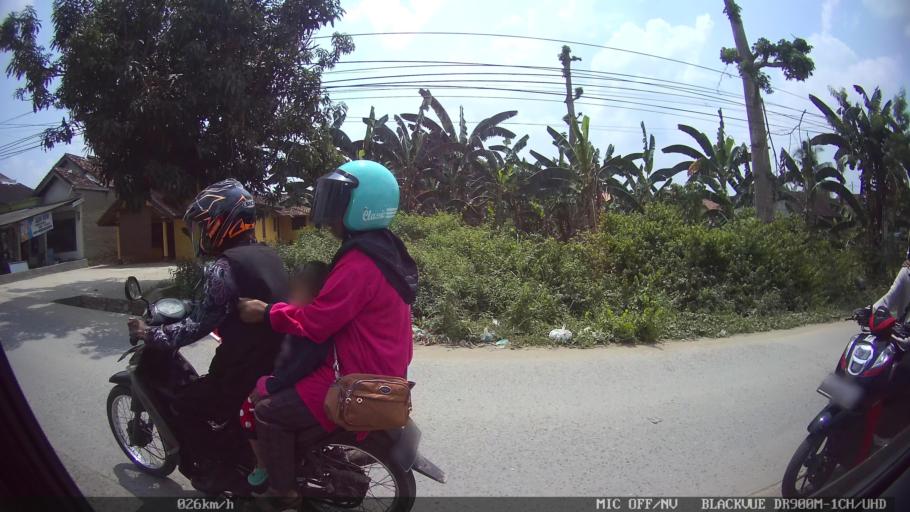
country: ID
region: Lampung
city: Pringsewu
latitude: -5.3446
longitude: 104.9750
